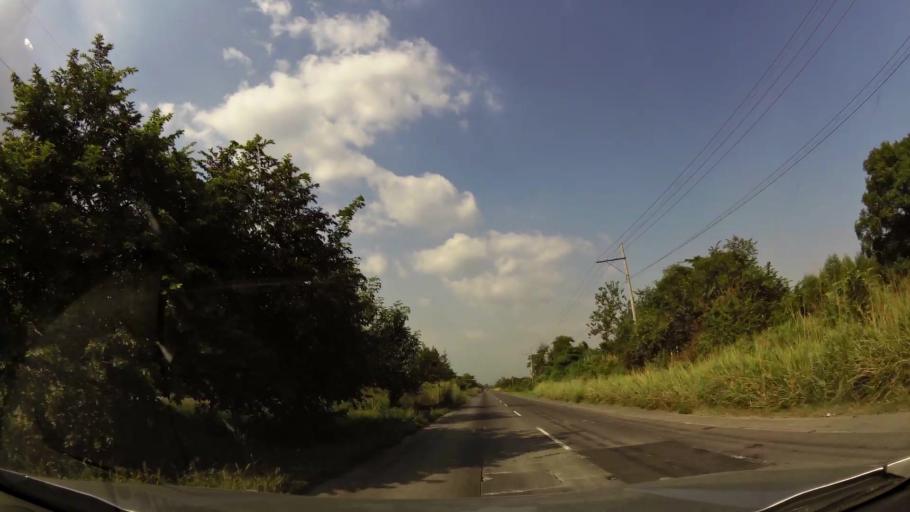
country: GT
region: Escuintla
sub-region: Municipio de Masagua
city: Masagua
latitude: 14.1166
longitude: -90.7815
